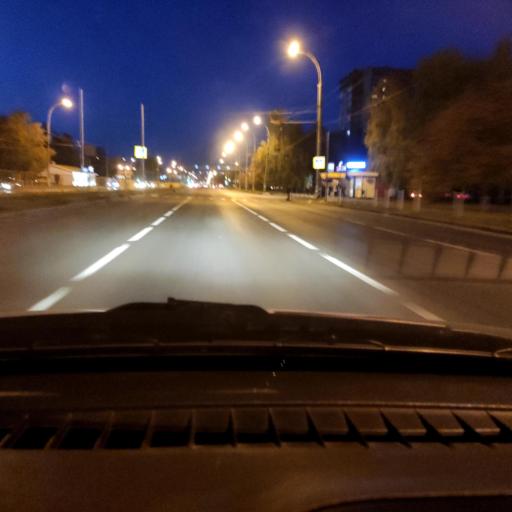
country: RU
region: Samara
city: Tol'yatti
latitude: 53.5336
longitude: 49.2986
